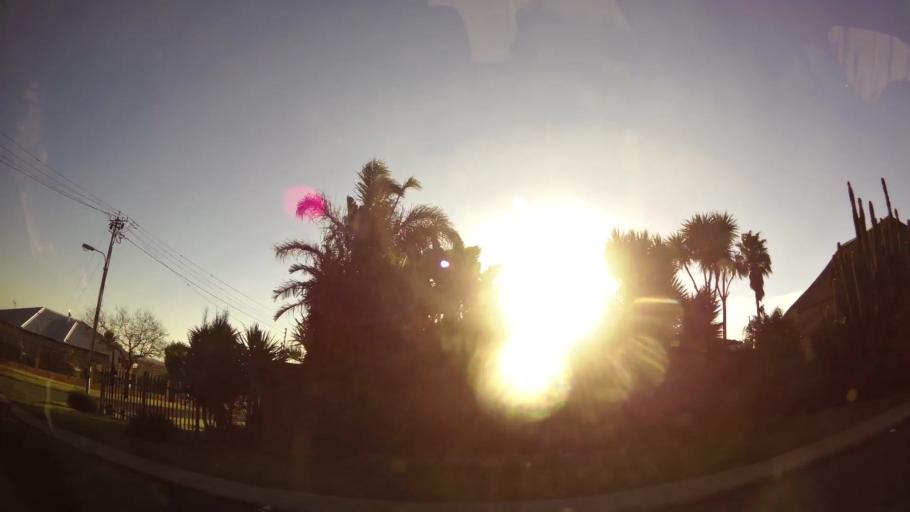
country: ZA
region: Gauteng
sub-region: City of Johannesburg Metropolitan Municipality
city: Roodepoort
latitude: -26.1747
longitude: 27.9392
